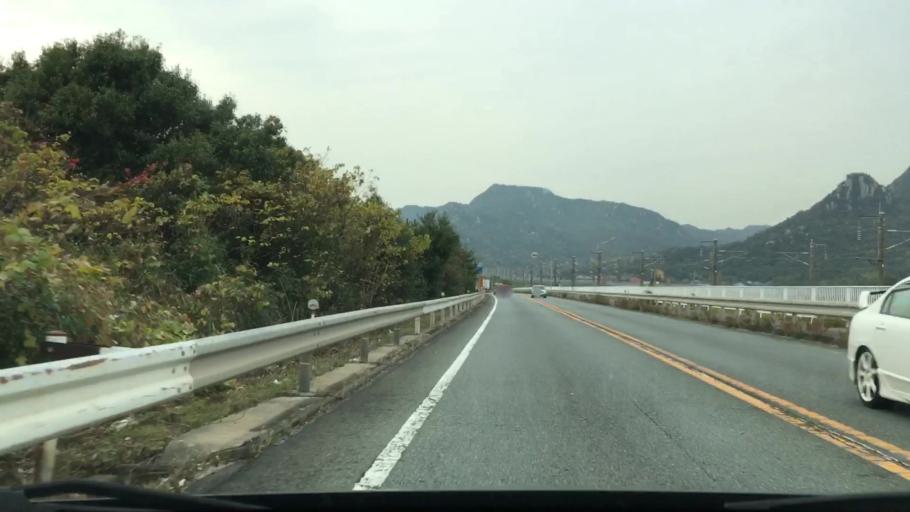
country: JP
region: Yamaguchi
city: Hofu
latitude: 34.0741
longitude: 131.5734
